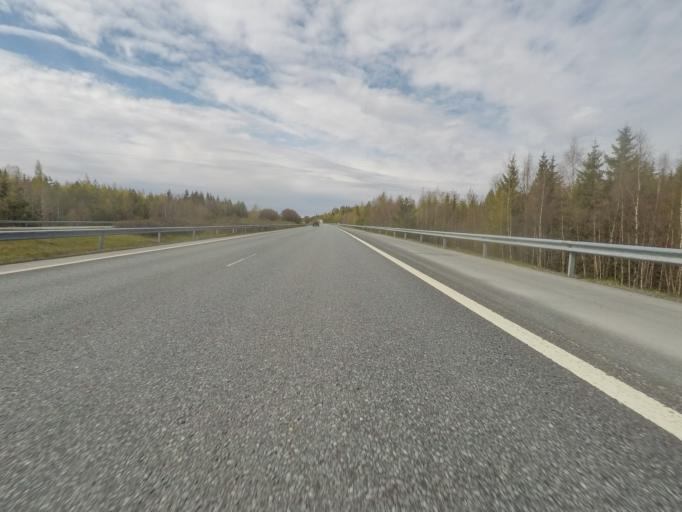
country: FI
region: Haeme
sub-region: Haemeenlinna
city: Kalvola
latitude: 61.1244
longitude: 24.1186
